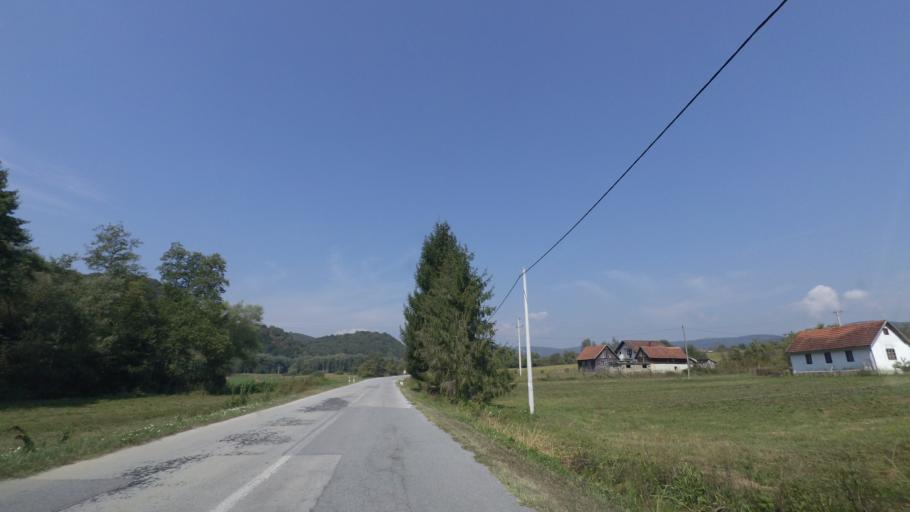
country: HR
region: Sisacko-Moslavacka
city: Dvor
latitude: 45.1202
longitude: 16.2594
